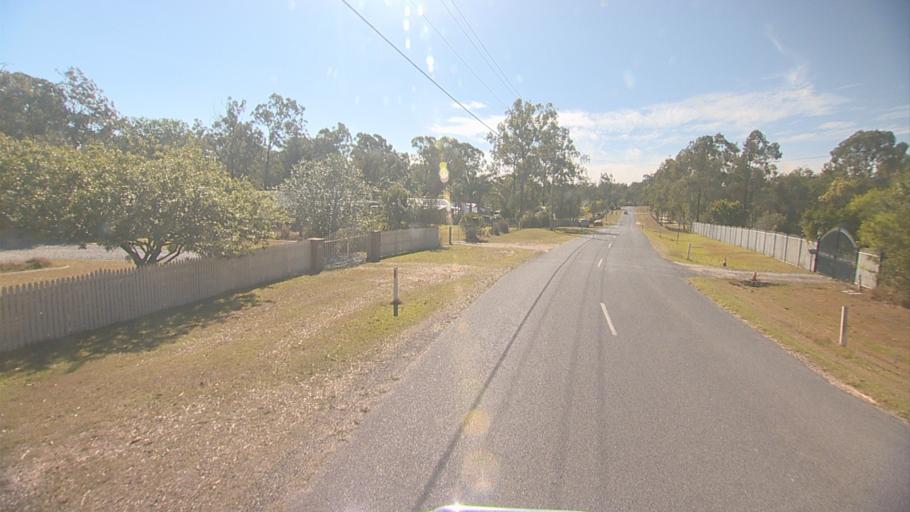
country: AU
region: Queensland
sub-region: Logan
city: North Maclean
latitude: -27.7302
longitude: 152.9614
